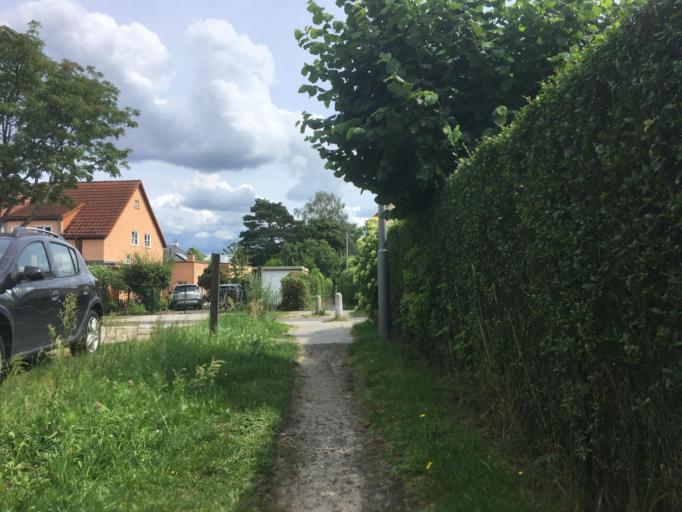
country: DE
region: Berlin
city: Mahlsdorf
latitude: 52.5084
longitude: 13.6007
